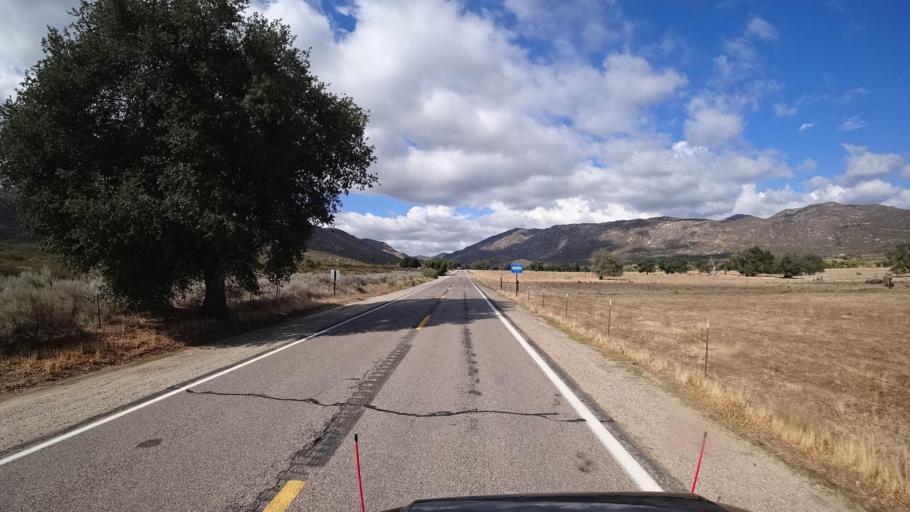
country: US
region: California
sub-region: San Diego County
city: Pine Valley
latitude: 32.7500
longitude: -116.4938
